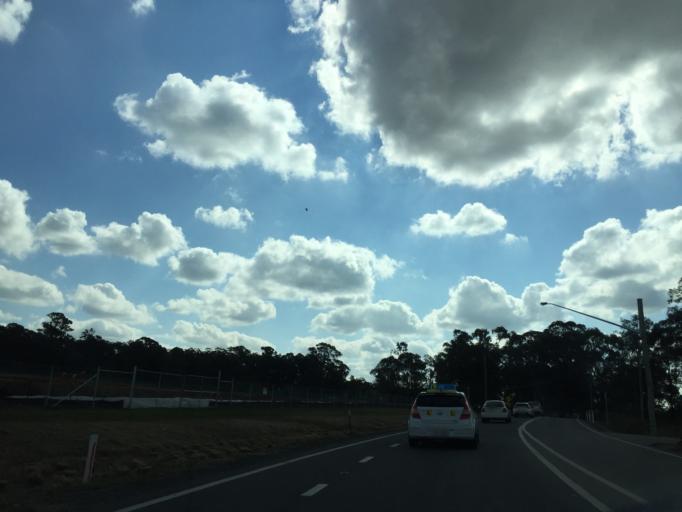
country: AU
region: New South Wales
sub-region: Blacktown
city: Rouse Hill
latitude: -33.6930
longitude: 150.9074
